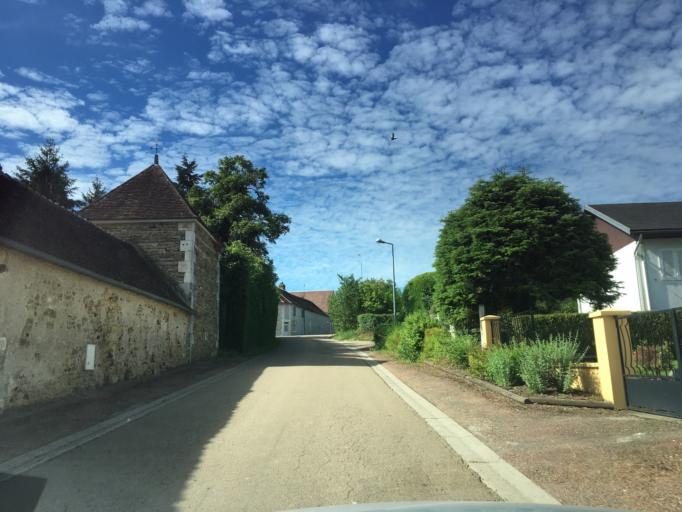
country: FR
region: Bourgogne
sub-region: Departement de l'Yonne
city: Saint-Georges-sur-Baulche
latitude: 47.7844
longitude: 3.5038
